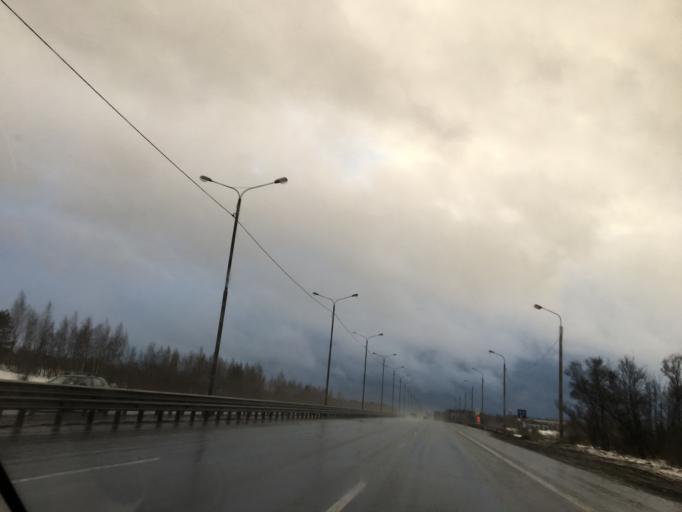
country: RU
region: Moskovskaya
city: Novyy Byt
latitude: 55.0758
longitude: 37.5736
